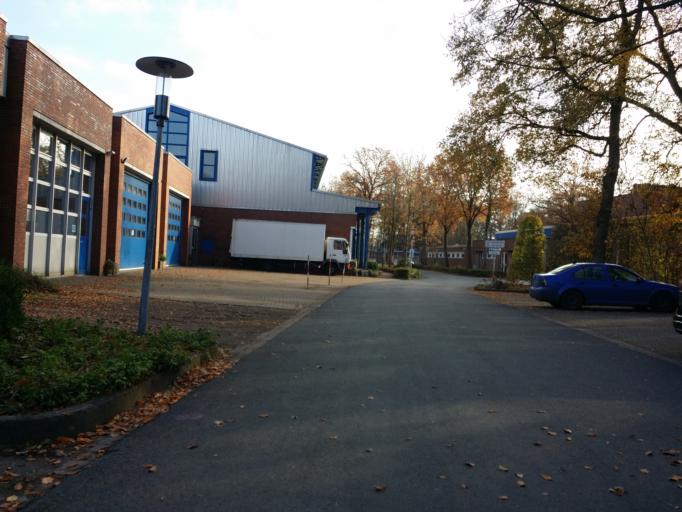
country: DE
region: Lower Saxony
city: Rotenburg
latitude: 53.0973
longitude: 9.3739
